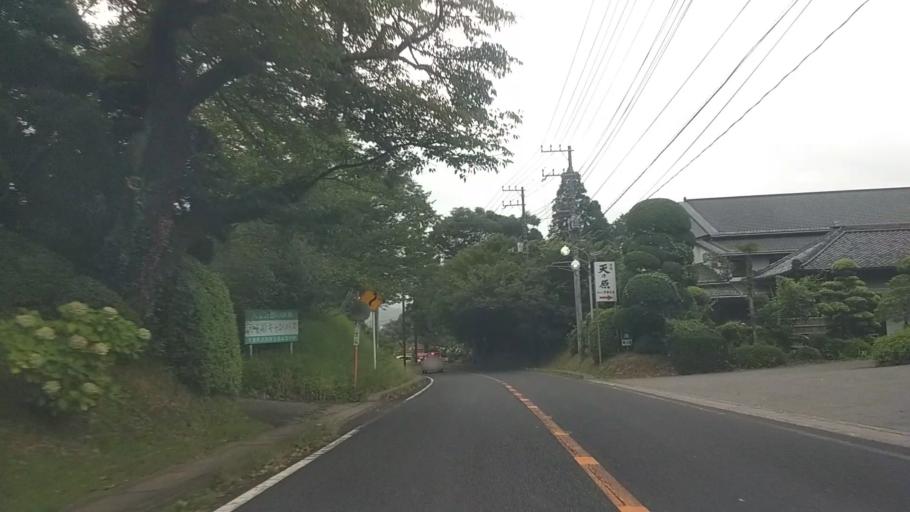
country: JP
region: Chiba
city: Kisarazu
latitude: 35.3010
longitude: 140.0733
